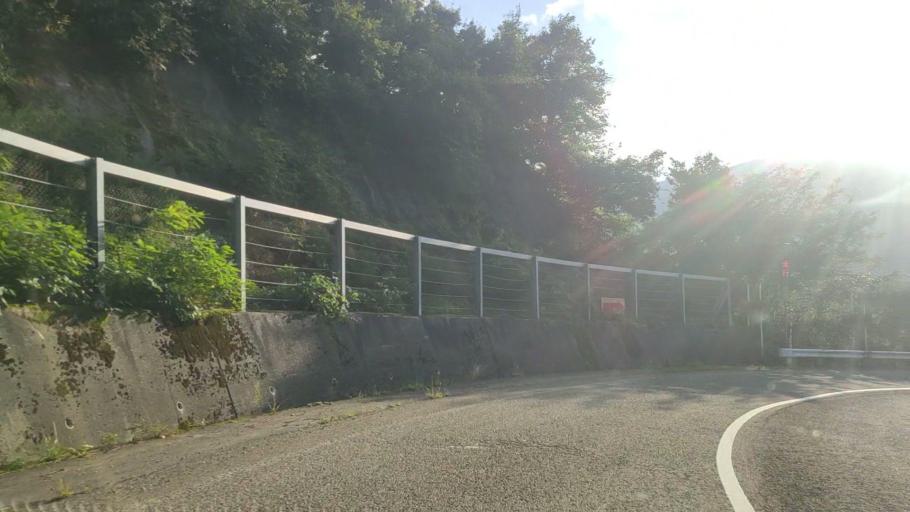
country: JP
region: Toyama
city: Yatsuomachi-higashikumisaka
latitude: 36.4534
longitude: 137.0293
